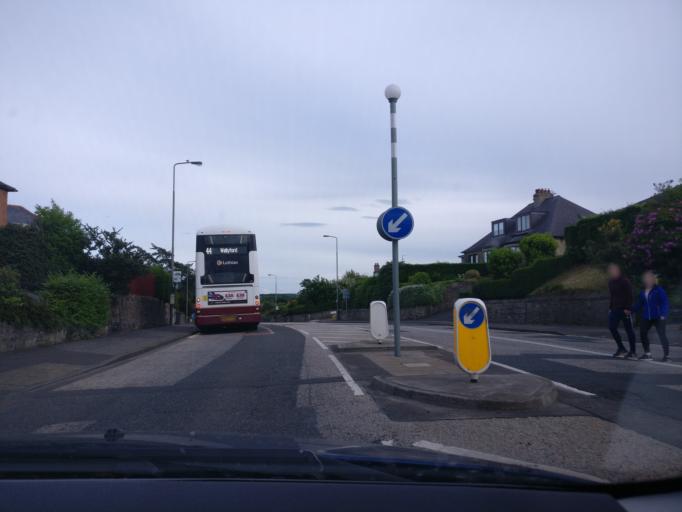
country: GB
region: Scotland
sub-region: West Lothian
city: Seafield
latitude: 55.9504
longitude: -3.1406
